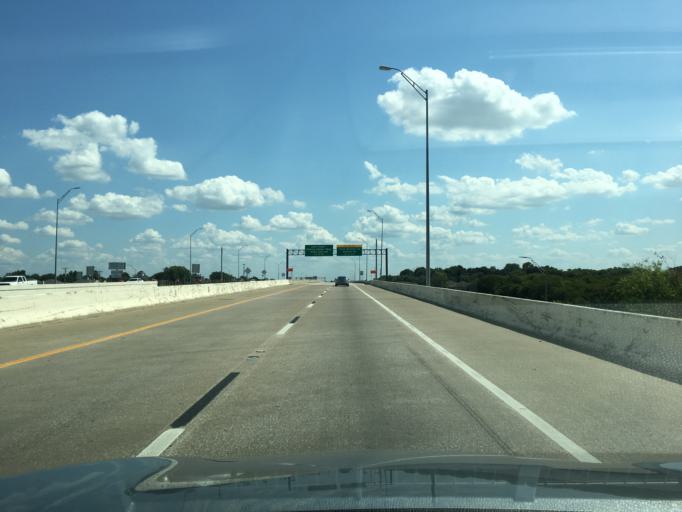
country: US
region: Texas
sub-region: Tarrant County
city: Arlington
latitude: 32.6615
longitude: -97.0627
